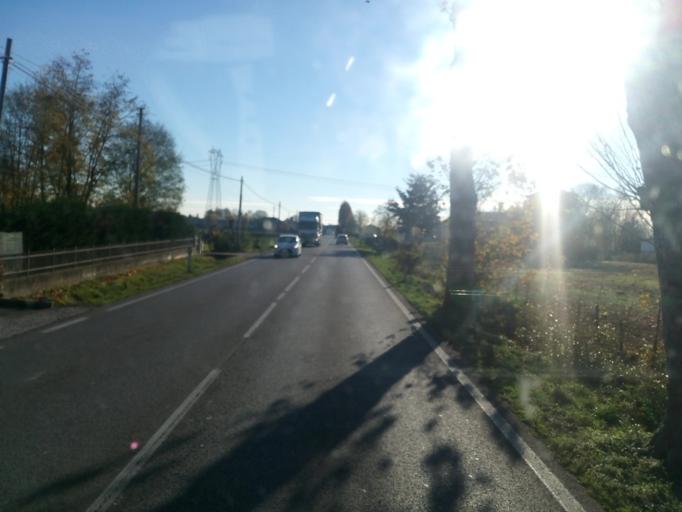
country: IT
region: Veneto
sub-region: Provincia di Padova
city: Galliera Veneta
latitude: 45.6949
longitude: 11.8394
